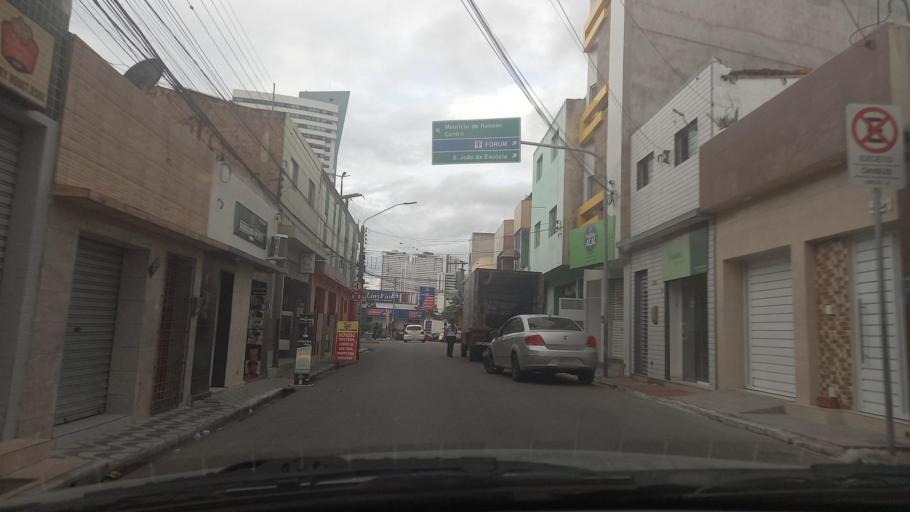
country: BR
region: Pernambuco
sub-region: Caruaru
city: Caruaru
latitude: -8.2755
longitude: -35.9655
